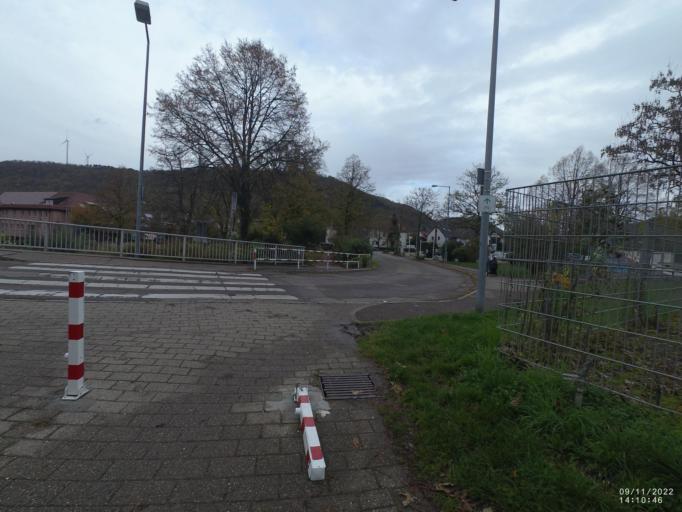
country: DE
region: Baden-Wuerttemberg
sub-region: Regierungsbezirk Stuttgart
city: Geislingen an der Steige
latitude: 48.6242
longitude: 9.8193
